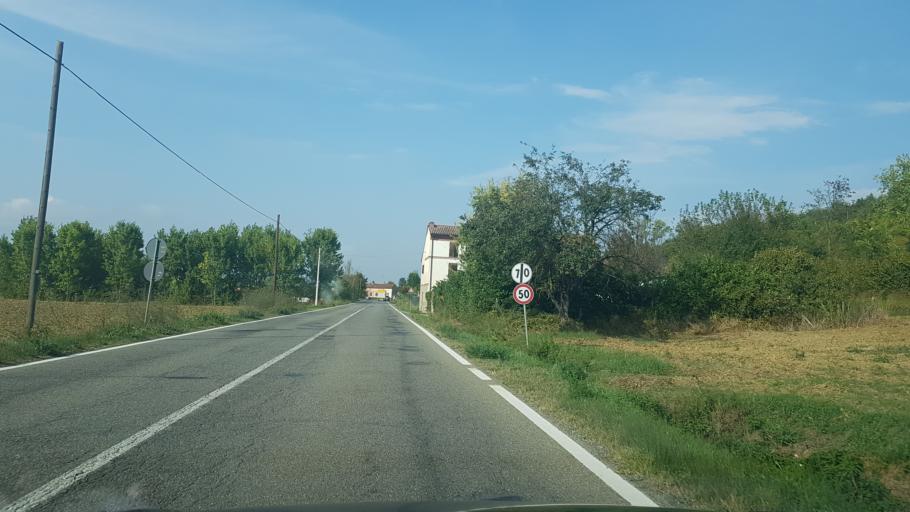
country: IT
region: Piedmont
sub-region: Provincia di Alessandria
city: Bergamasco
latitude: 44.8141
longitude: 8.4578
